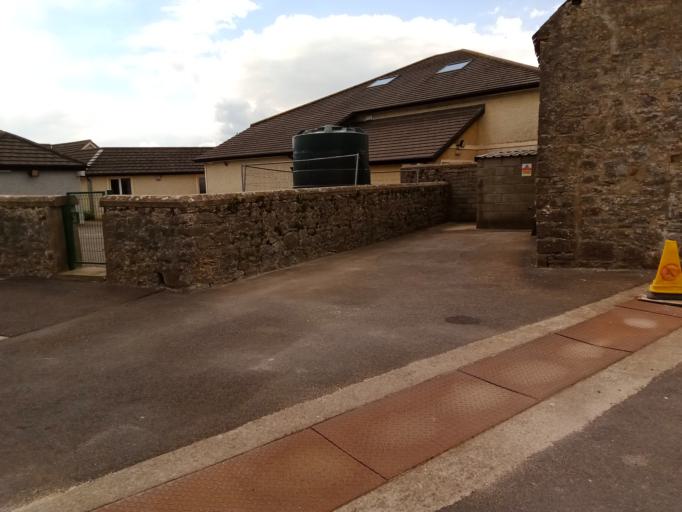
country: IE
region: Leinster
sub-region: Kilkenny
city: Kilkenny
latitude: 52.6003
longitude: -7.3082
